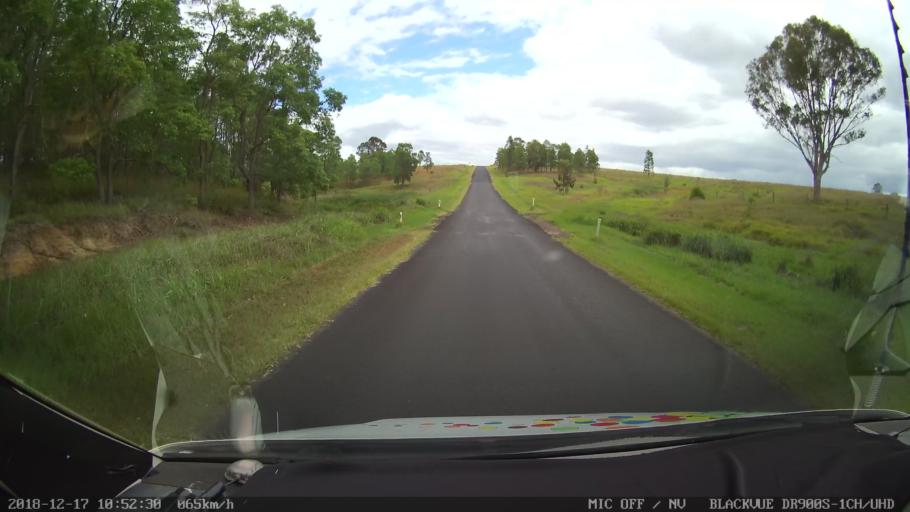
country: AU
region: New South Wales
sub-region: Tenterfield Municipality
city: Carrolls Creek
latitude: -28.8448
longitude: 152.5633
